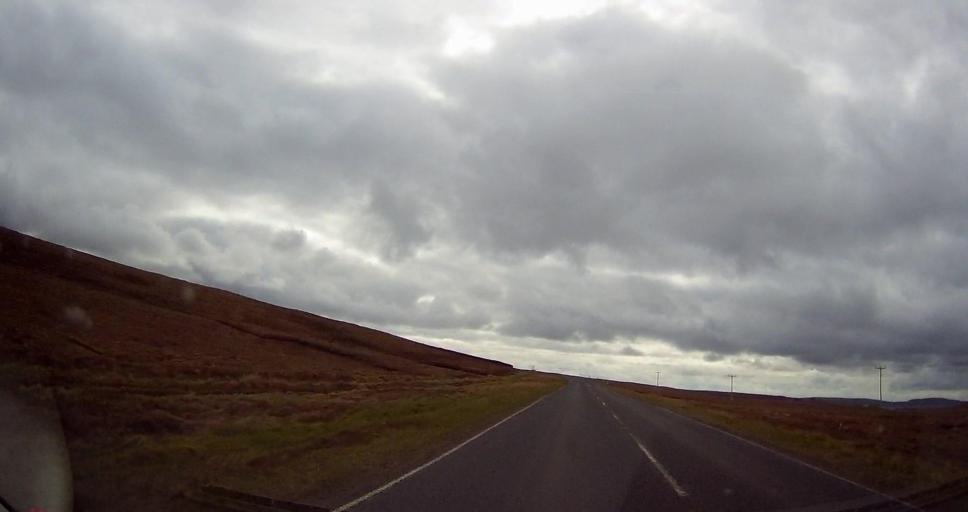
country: GB
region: Scotland
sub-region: Shetland Islands
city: Shetland
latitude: 60.6654
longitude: -1.0283
